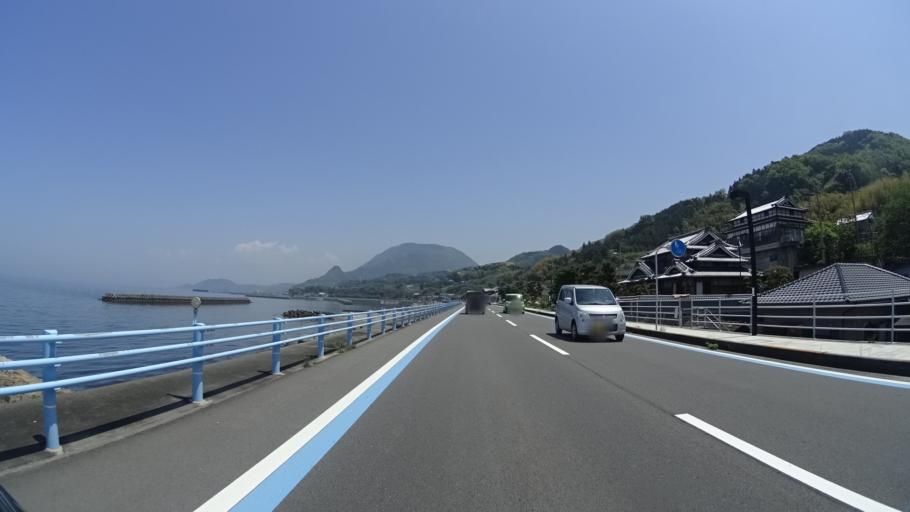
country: JP
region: Ehime
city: Iyo
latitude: 33.6782
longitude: 132.6214
